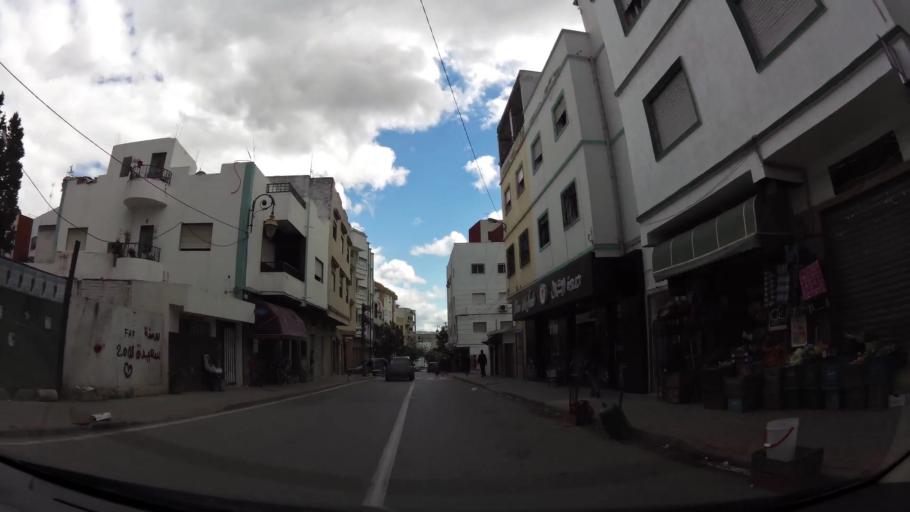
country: MA
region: Tanger-Tetouan
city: Tetouan
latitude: 35.5807
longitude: -5.3525
